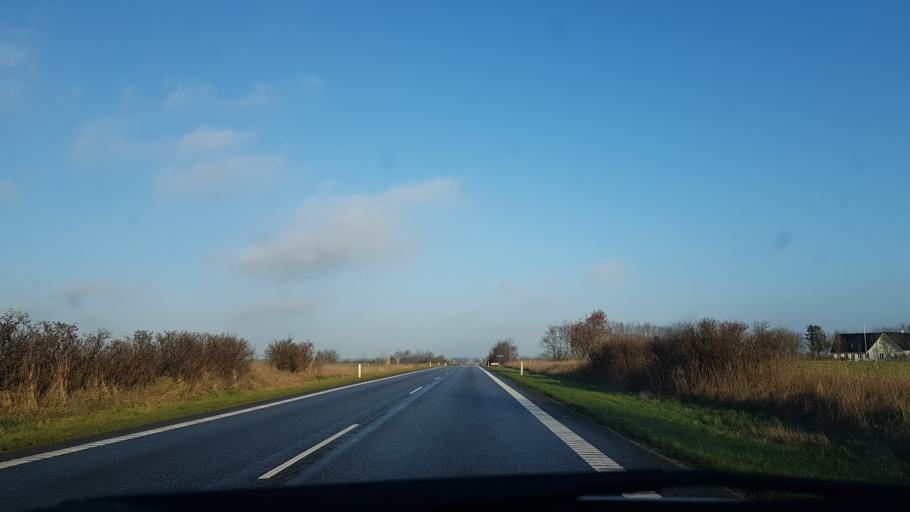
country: DK
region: South Denmark
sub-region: Tonder Kommune
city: Toftlund
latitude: 55.2125
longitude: 9.0981
